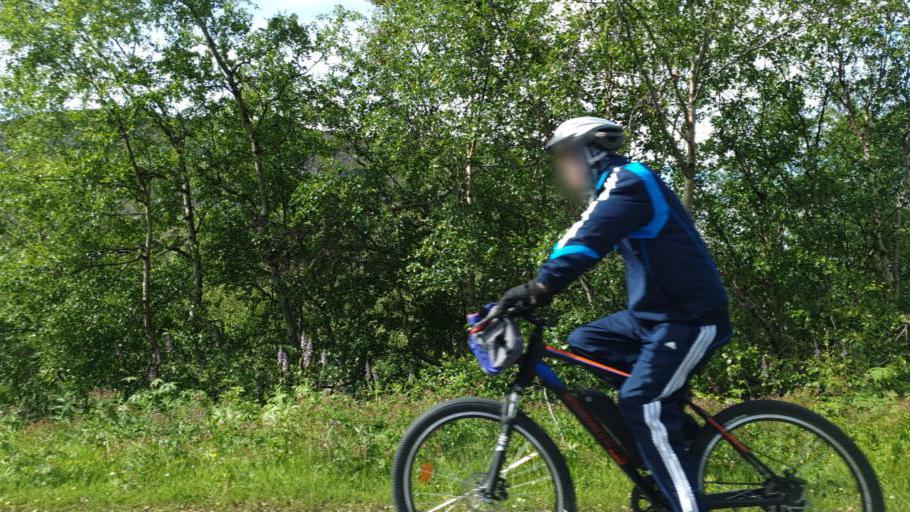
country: NO
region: Oppland
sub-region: Lom
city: Fossbergom
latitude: 61.4923
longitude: 8.8164
